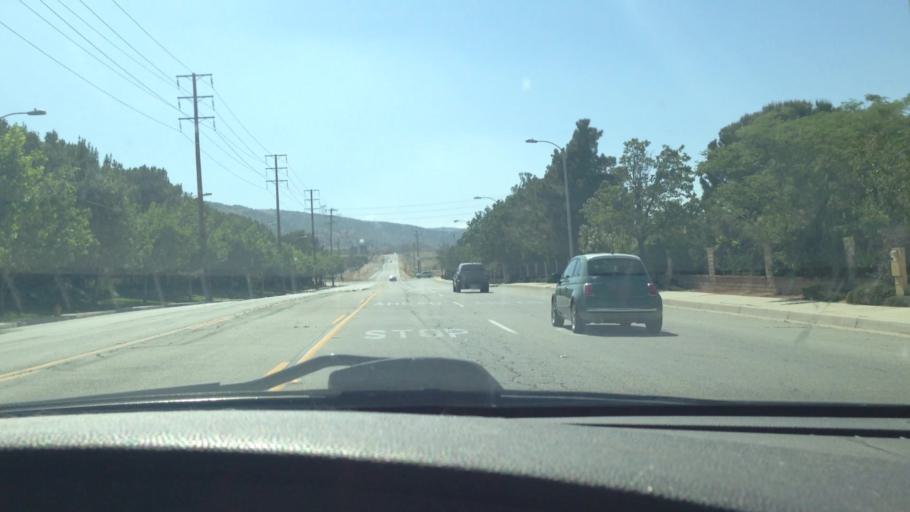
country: US
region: California
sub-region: Los Angeles County
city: Quartz Hill
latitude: 34.6309
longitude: -118.2334
